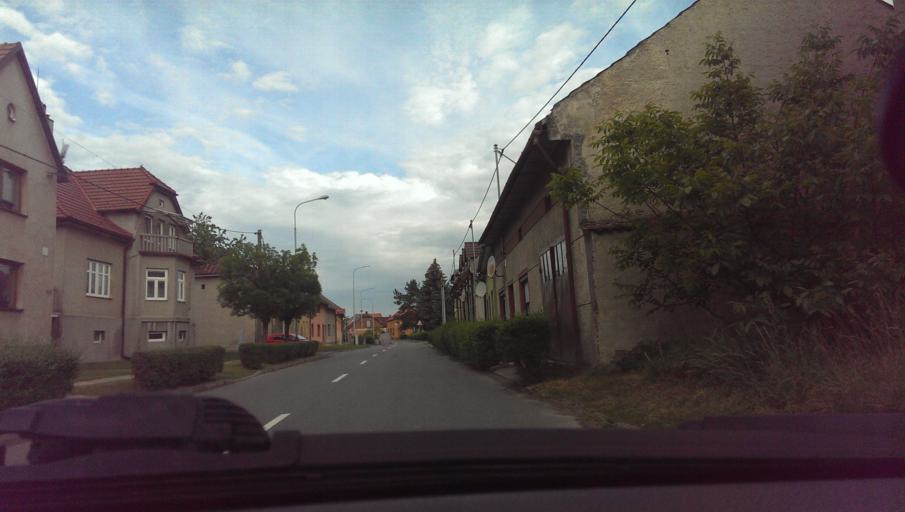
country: CZ
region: Zlin
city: Kvasice
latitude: 49.2367
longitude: 17.4762
